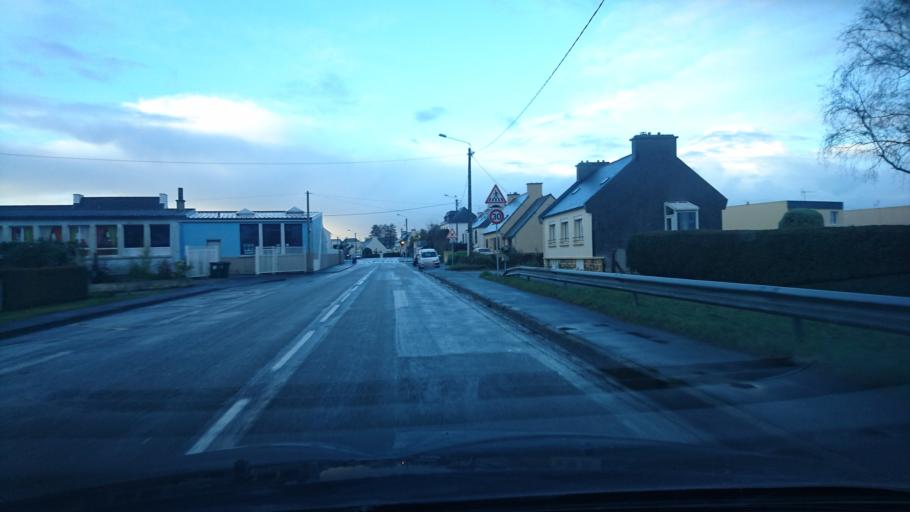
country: FR
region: Brittany
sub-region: Departement du Finistere
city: Guilers
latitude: 48.4201
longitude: -4.5589
